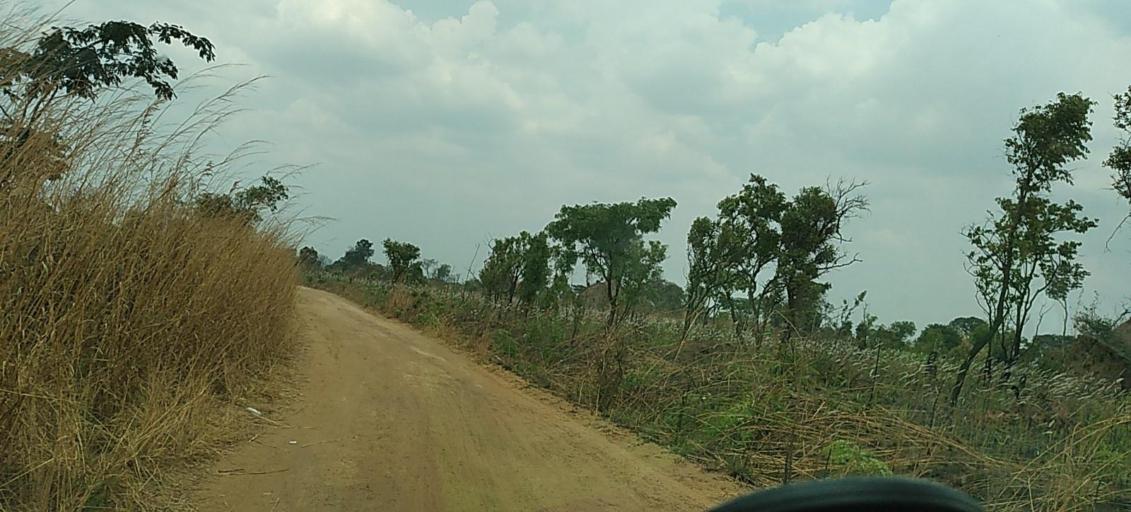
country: ZM
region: North-Western
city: Kansanshi
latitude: -12.0841
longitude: 26.3660
